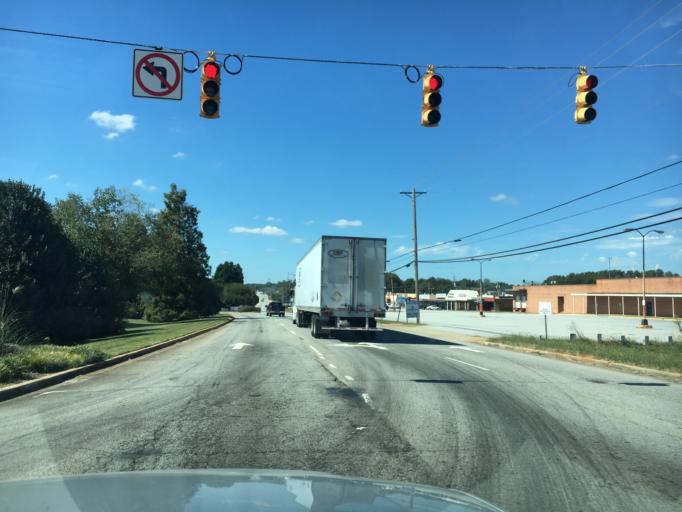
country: US
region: South Carolina
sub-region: Pickens County
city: Easley
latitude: 34.8262
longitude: -82.5641
